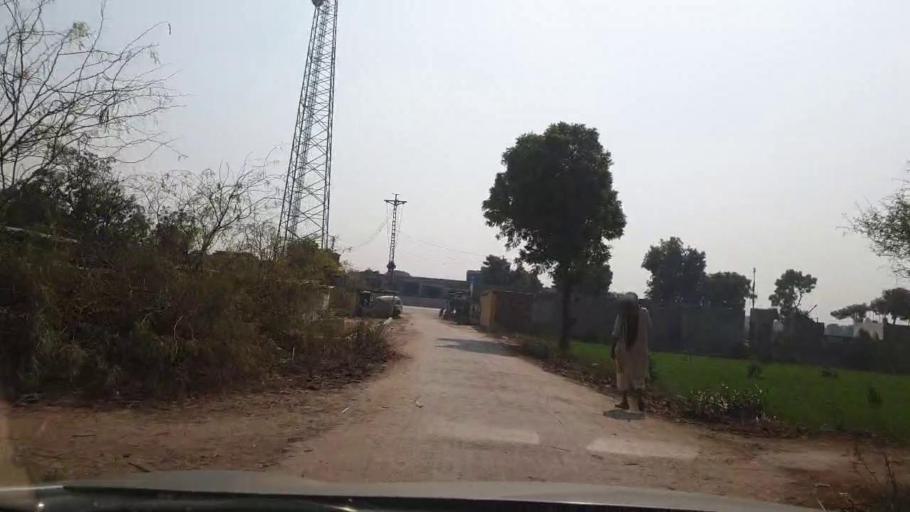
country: PK
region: Sindh
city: Tando Allahyar
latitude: 25.4791
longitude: 68.7720
